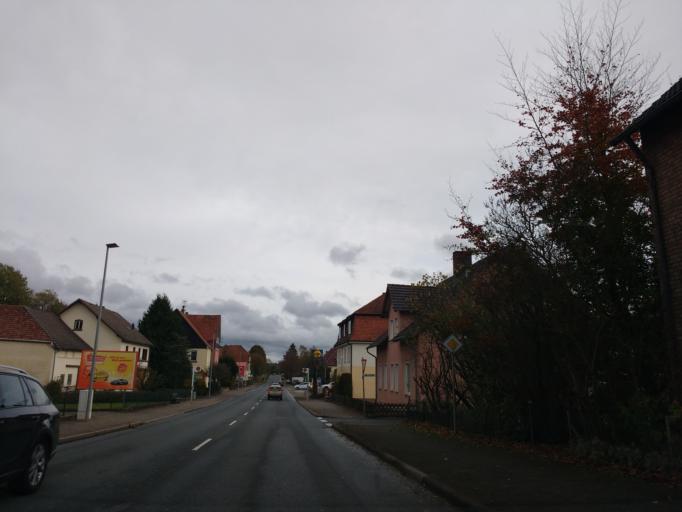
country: DE
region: Hesse
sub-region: Regierungsbezirk Kassel
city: Sachsenhausen
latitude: 51.2428
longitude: 9.0120
